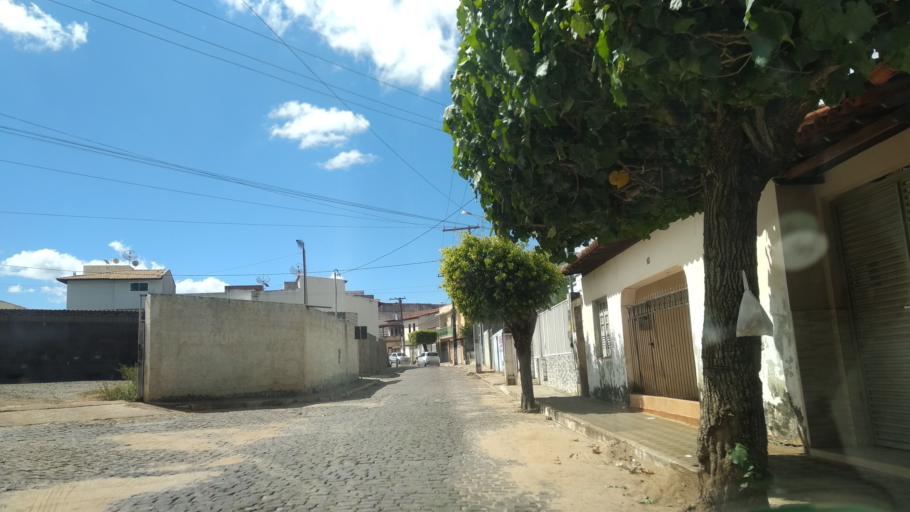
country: BR
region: Bahia
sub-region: Caetite
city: Caetite
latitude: -14.0668
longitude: -42.4868
